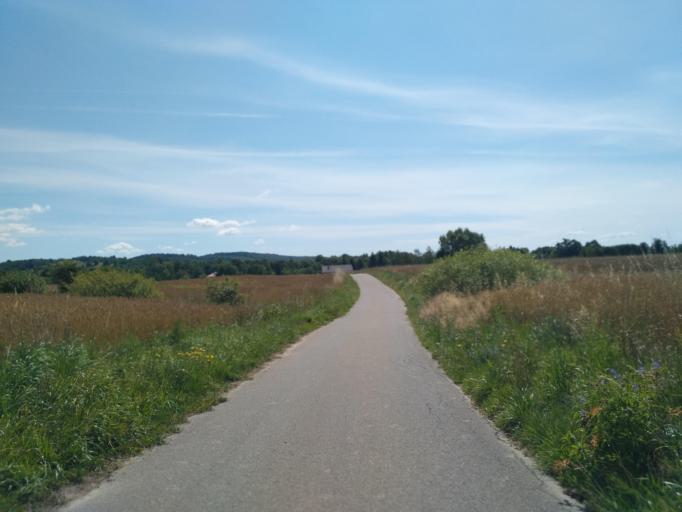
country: PL
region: Subcarpathian Voivodeship
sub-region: Powiat brzozowski
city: Jablonica Polska
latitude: 49.6904
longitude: 21.8797
